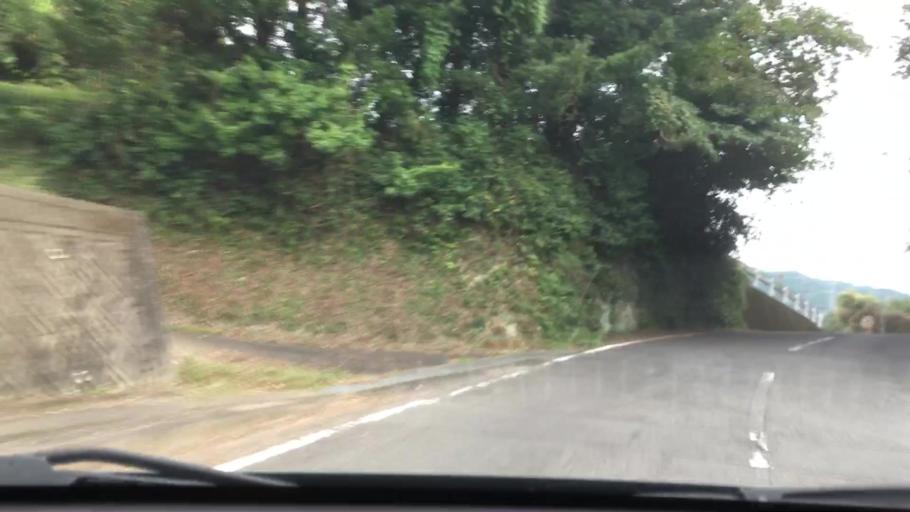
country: JP
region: Nagasaki
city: Sasebo
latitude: 33.0039
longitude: 129.7640
